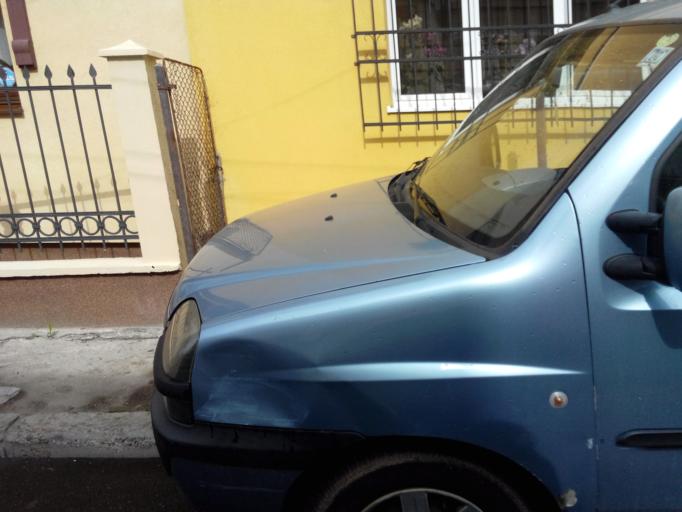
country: RO
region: Bucuresti
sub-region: Municipiul Bucuresti
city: Bucuresti
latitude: 44.4239
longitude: 26.0999
